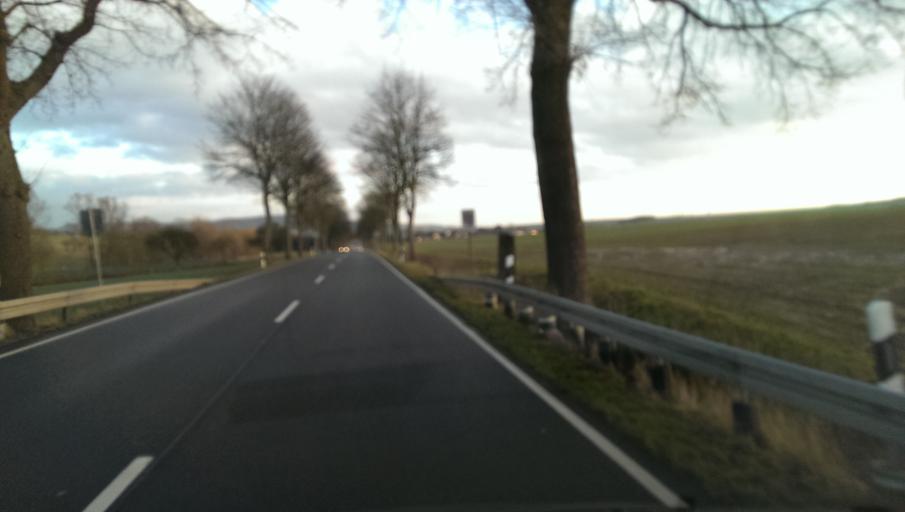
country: DE
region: Lower Saxony
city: Eimen
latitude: 51.8754
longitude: 9.7972
